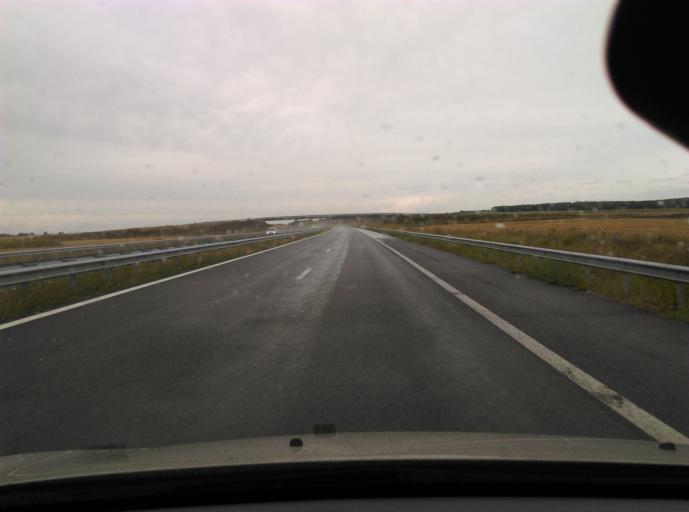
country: BG
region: Khaskovo
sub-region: Obshtina Dimitrovgrad
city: Dimitrovgrad
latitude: 42.0371
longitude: 25.5376
